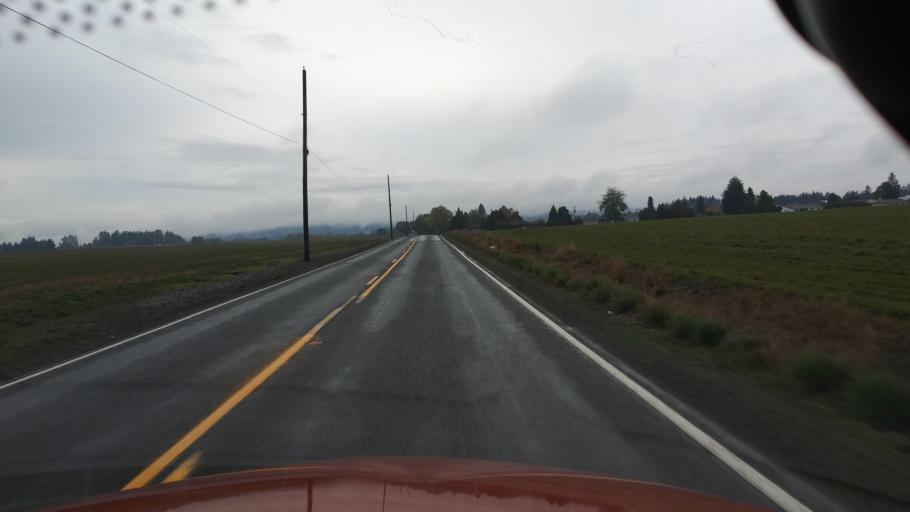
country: US
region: Oregon
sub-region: Washington County
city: North Plains
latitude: 45.5868
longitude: -123.0172
